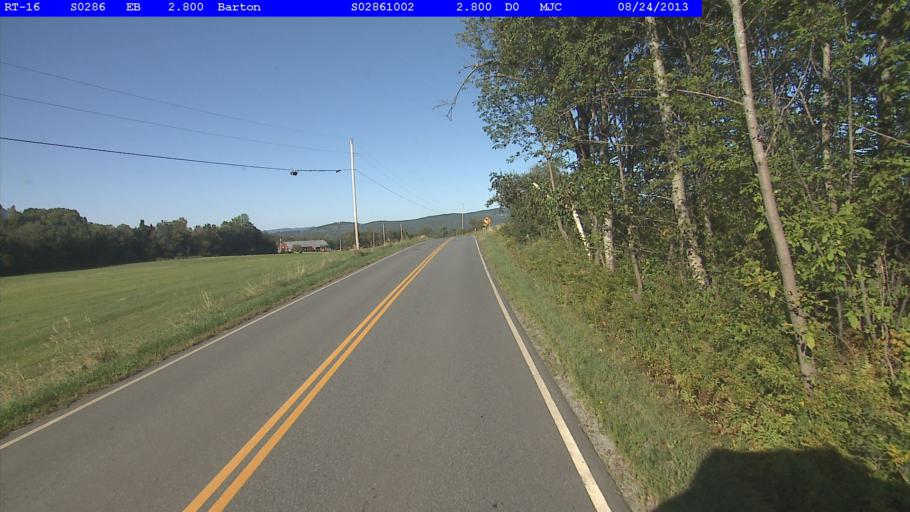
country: US
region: Vermont
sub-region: Orleans County
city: Newport
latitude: 44.7637
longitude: -72.1307
